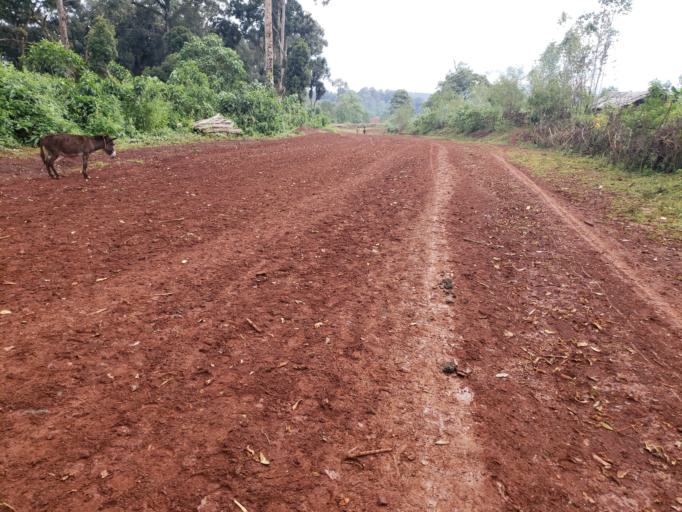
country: ET
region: Oromiya
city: Dodola
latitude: 6.5547
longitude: 39.4233
